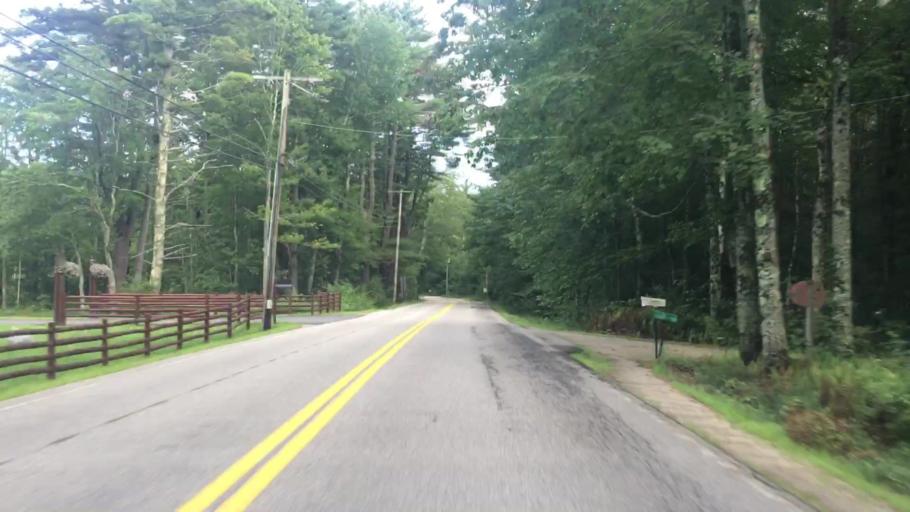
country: US
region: Maine
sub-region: York County
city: West Kennebunk
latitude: 43.4538
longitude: -70.6130
